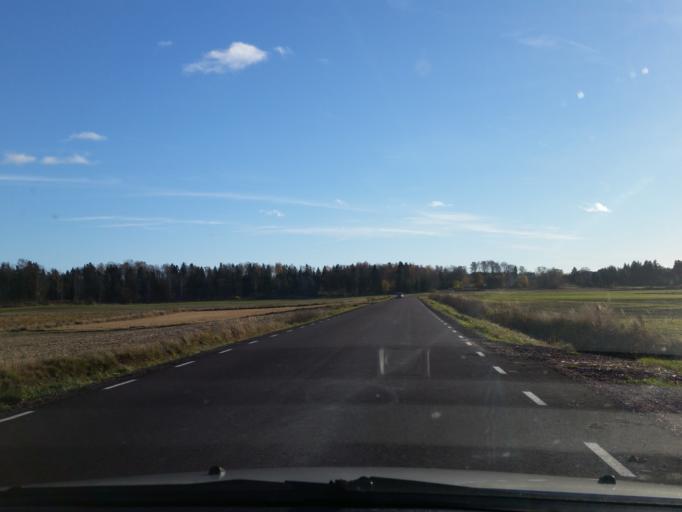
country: AX
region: Alands landsbygd
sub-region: Jomala
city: Jomala
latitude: 60.1954
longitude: 19.9589
